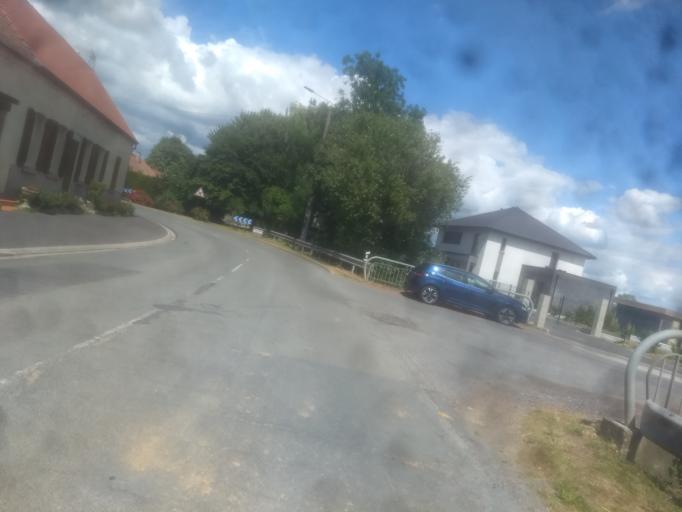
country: FR
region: Nord-Pas-de-Calais
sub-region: Departement du Pas-de-Calais
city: Croisilles
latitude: 50.2292
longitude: 2.8411
